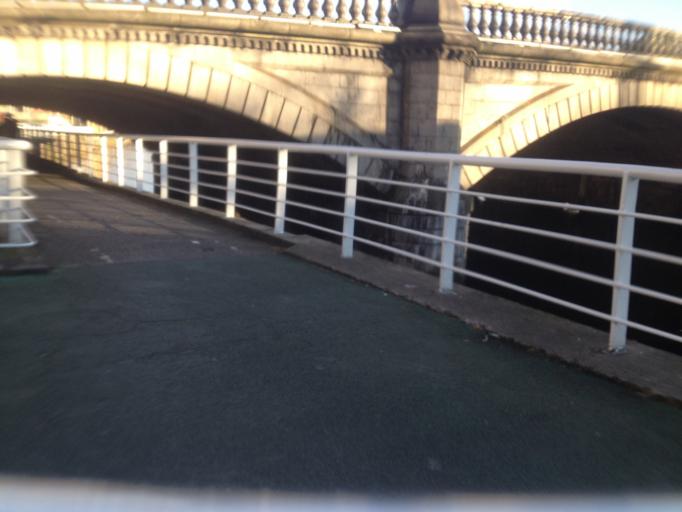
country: GB
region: Scotland
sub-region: Glasgow City
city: Glasgow
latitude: 55.8561
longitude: -4.2581
